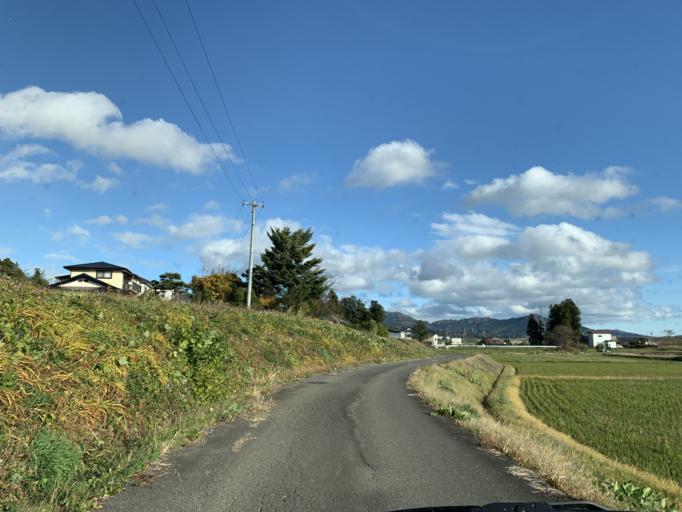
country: JP
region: Iwate
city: Ichinoseki
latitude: 39.0093
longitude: 141.1015
